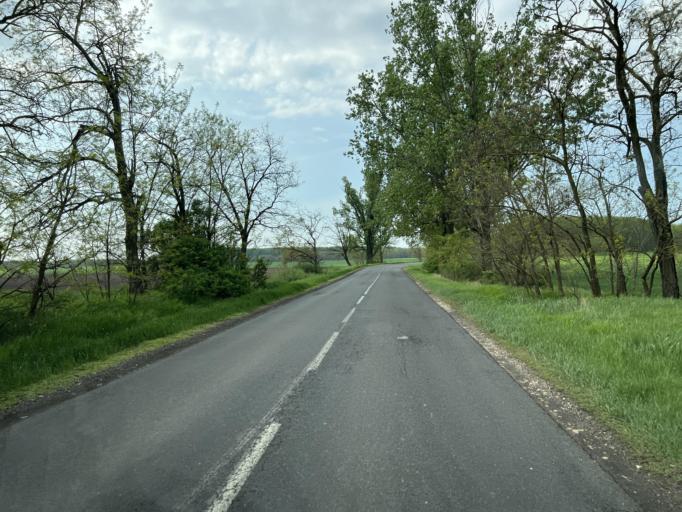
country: HU
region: Pest
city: Farmos
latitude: 47.3863
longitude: 19.8916
